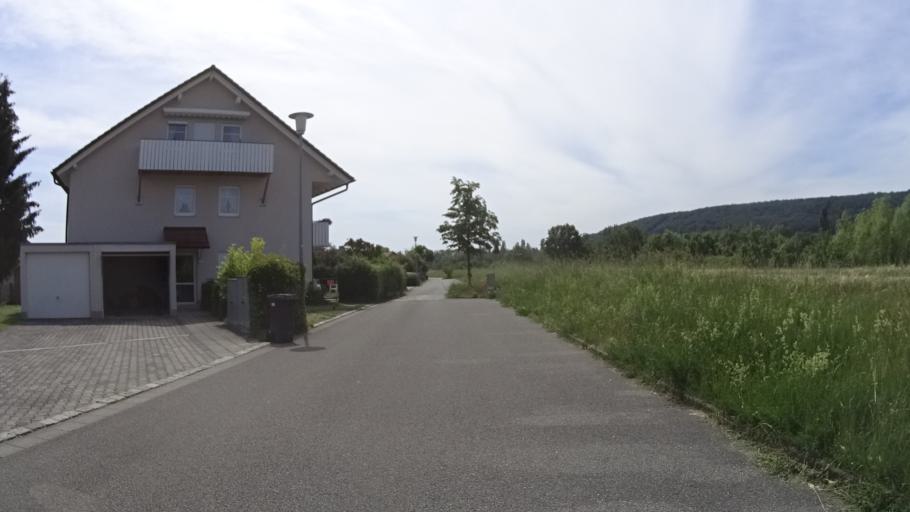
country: DE
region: Bavaria
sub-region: Lower Bavaria
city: Kelheim
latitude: 48.9150
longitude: 11.8819
